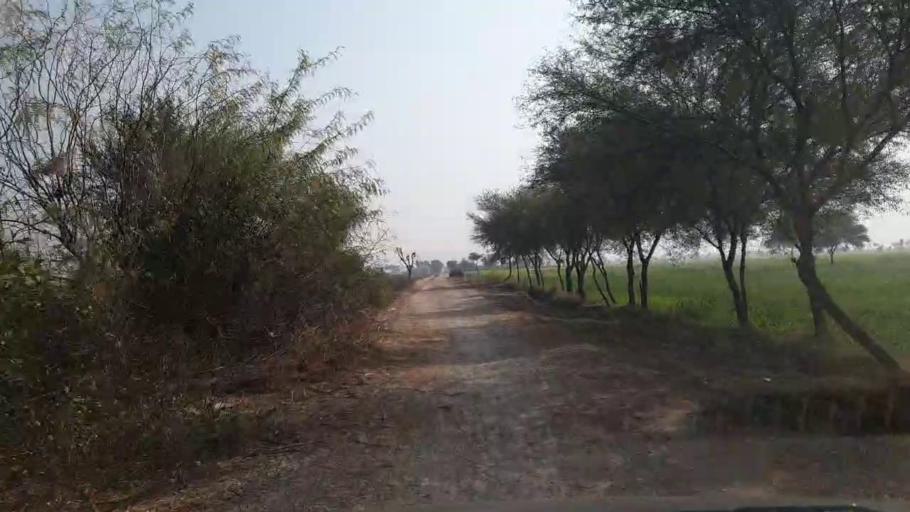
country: PK
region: Sindh
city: Hala
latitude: 25.9345
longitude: 68.4652
